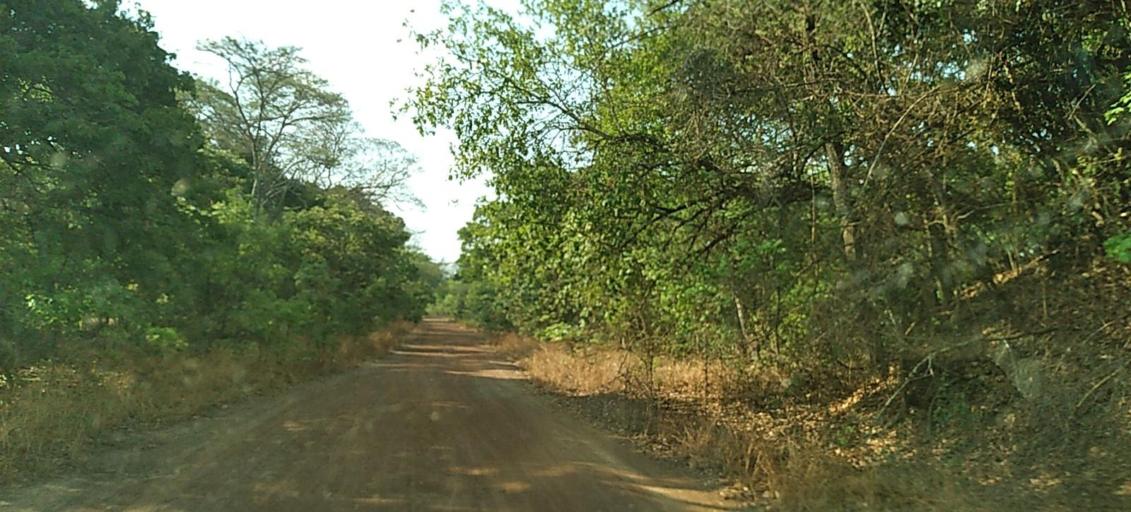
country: ZM
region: Copperbelt
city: Mpongwe
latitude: -13.4488
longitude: 28.0645
